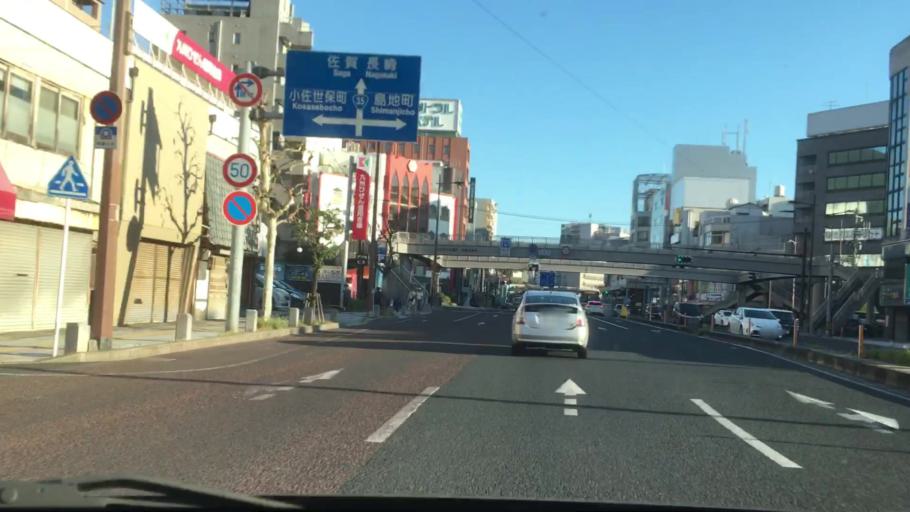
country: JP
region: Nagasaki
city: Sasebo
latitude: 33.1713
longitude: 129.7222
